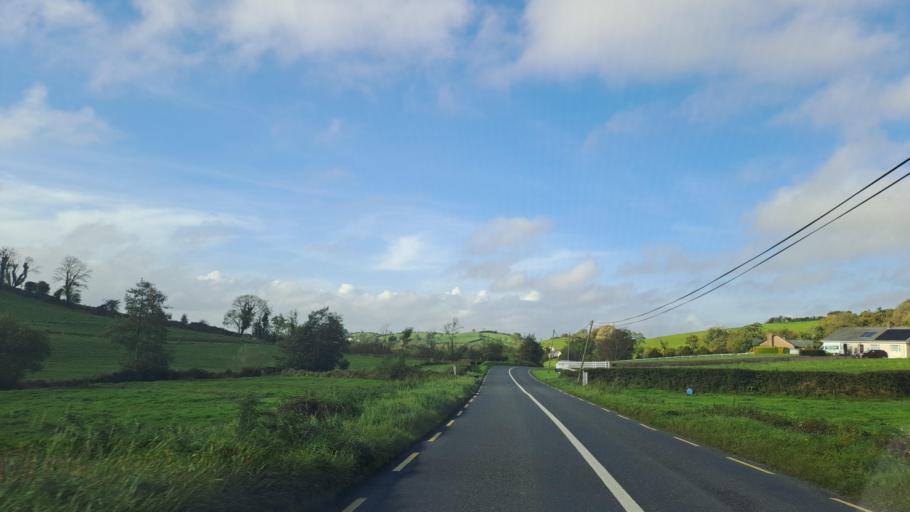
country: IE
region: Ulster
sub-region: An Cabhan
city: Cootehill
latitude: 54.0606
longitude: -7.0329
